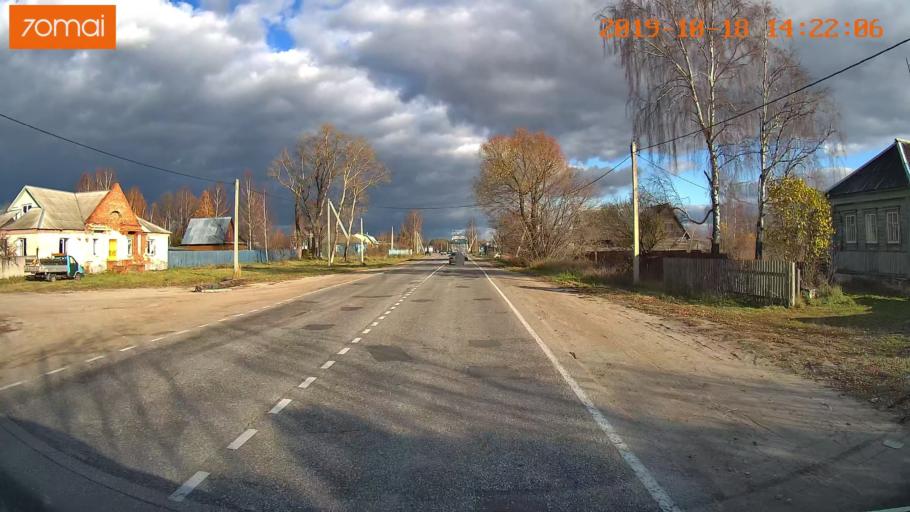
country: RU
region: Rjazan
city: Tuma
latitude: 55.1457
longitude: 40.4682
